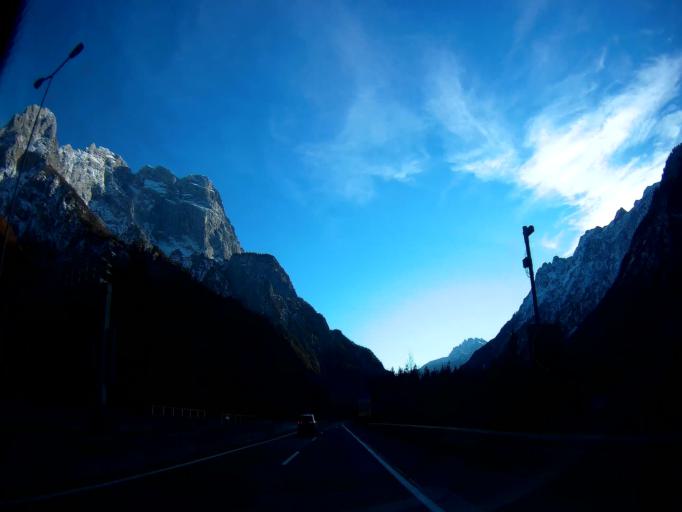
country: AT
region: Salzburg
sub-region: Politischer Bezirk Hallein
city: Golling an der Salzach
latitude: 47.5673
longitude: 13.1669
